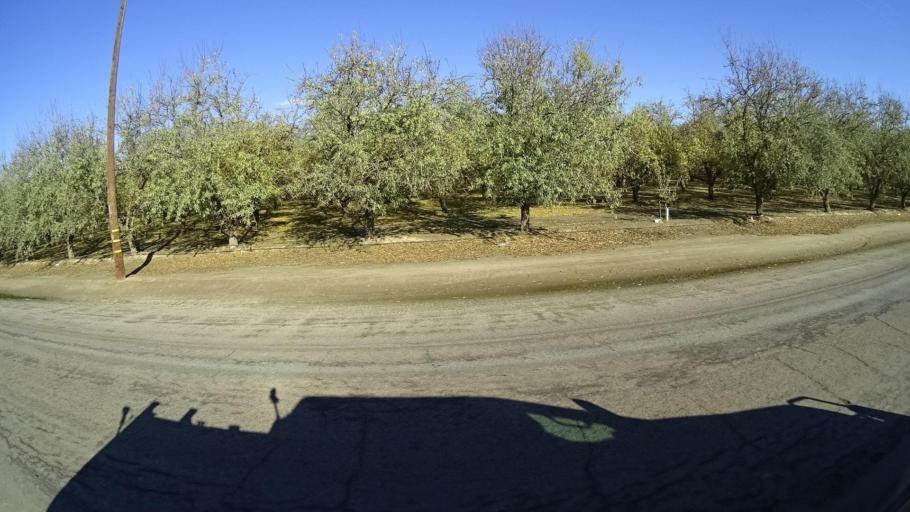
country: US
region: California
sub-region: Kern County
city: Delano
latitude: 35.7323
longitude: -119.2799
